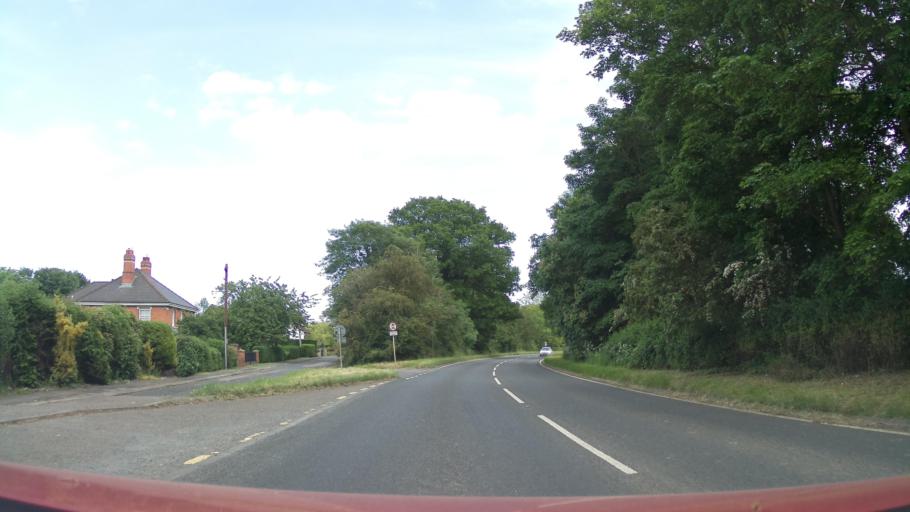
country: GB
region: England
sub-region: Worcestershire
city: Kempsey
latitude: 52.1642
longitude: -2.1653
